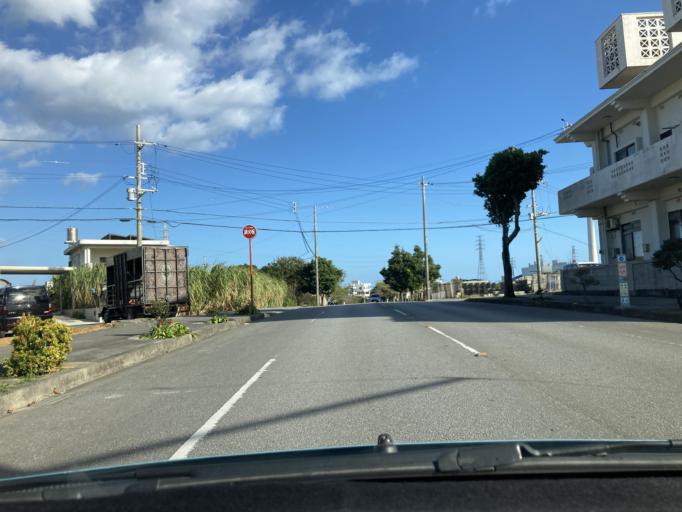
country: JP
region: Okinawa
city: Gushikawa
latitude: 26.3853
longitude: 127.8664
